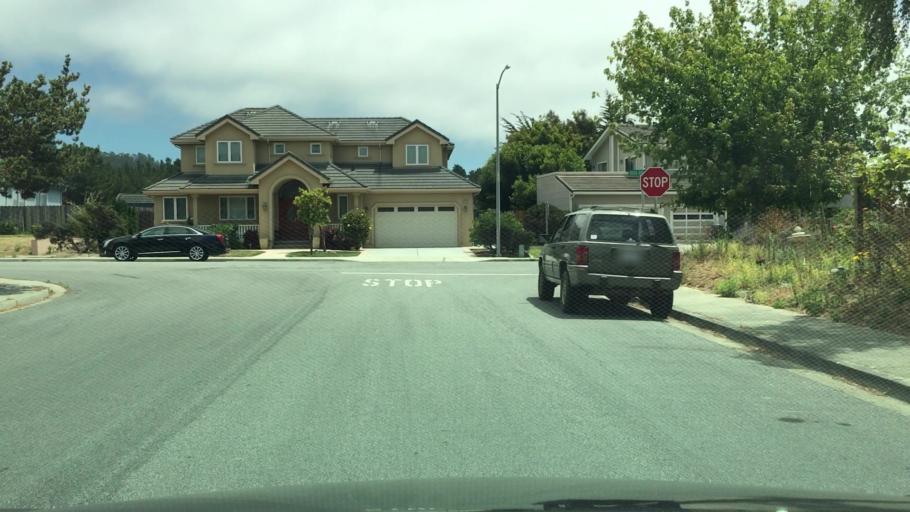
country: US
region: California
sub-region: San Mateo County
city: Half Moon Bay
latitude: 37.4740
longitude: -122.4326
